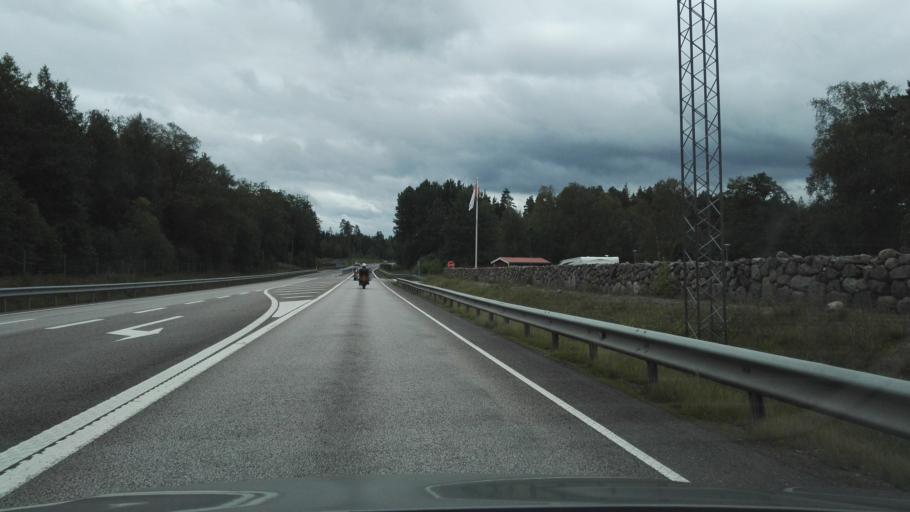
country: SE
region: Kronoberg
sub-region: Vaxjo Kommun
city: Rottne
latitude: 56.9784
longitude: 14.9820
